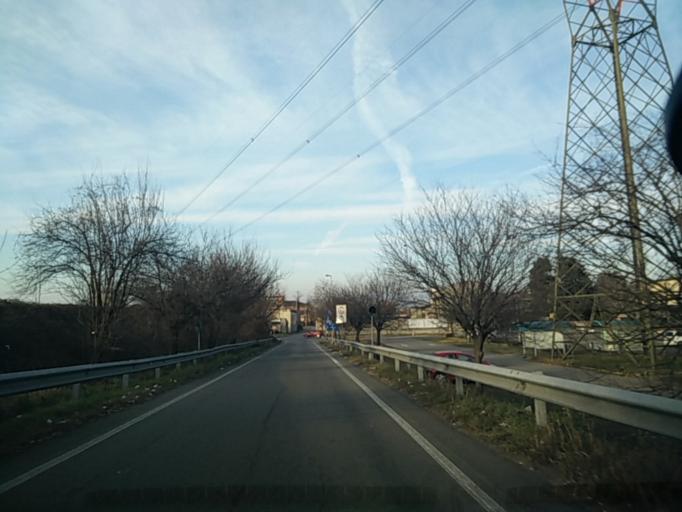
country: IT
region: Lombardy
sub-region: Provincia di Monza e Brianza
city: Cesano Maderno
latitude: 45.6284
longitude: 9.1636
